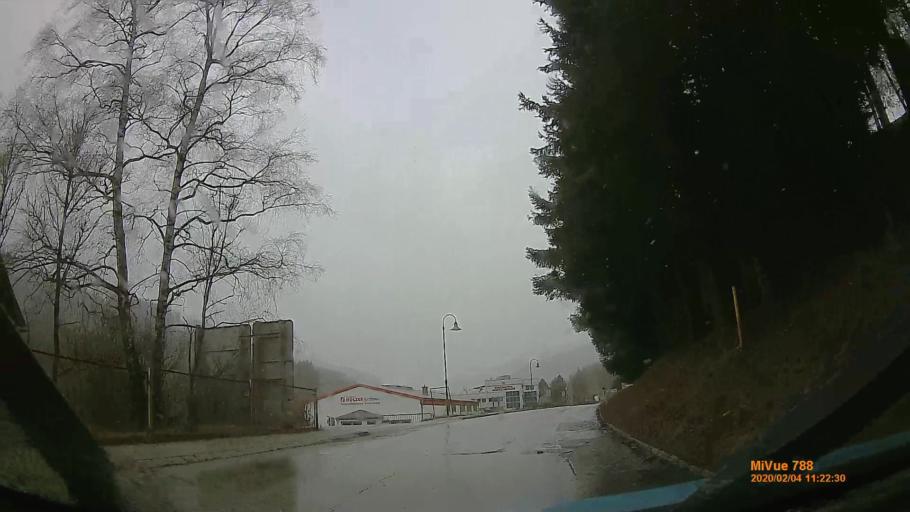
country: AT
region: Styria
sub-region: Politischer Bezirk Bruck-Muerzzuschlag
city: Muerzzuschlag
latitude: 47.6121
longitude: 15.6682
